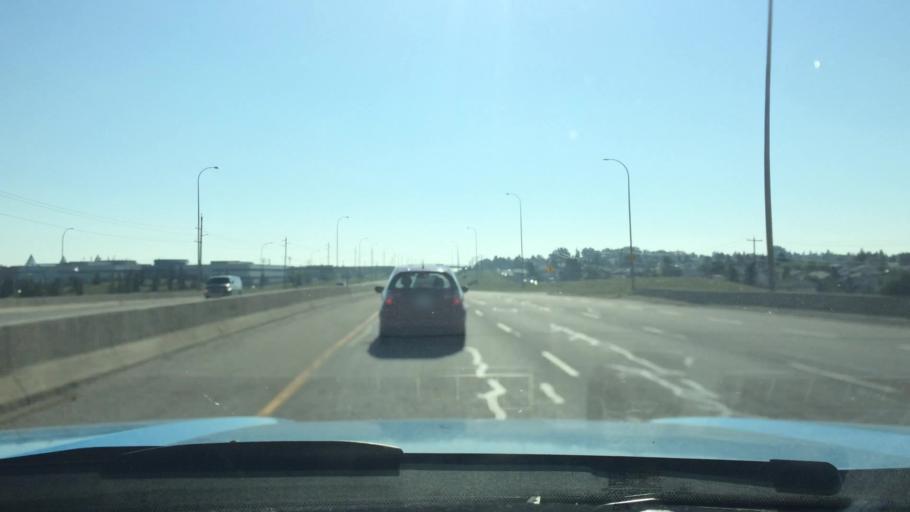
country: CA
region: Alberta
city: Calgary
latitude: 51.0958
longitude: -113.9811
